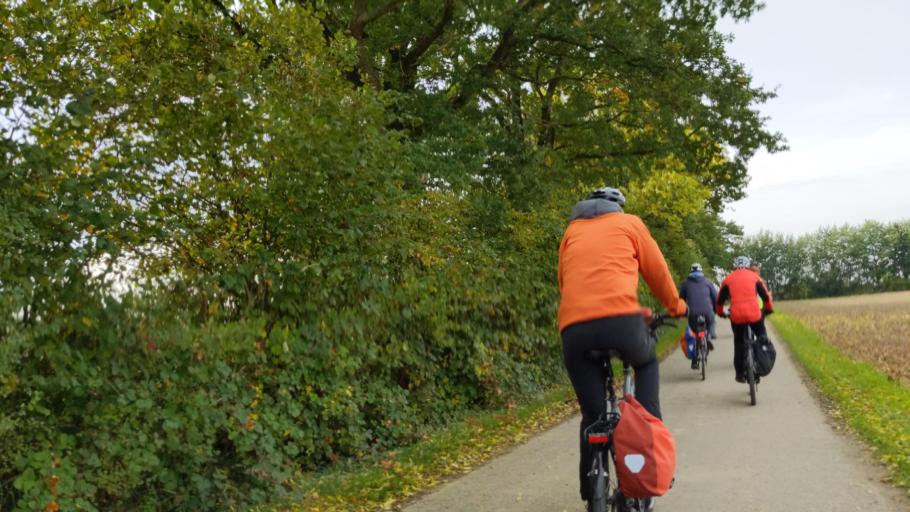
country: DE
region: Schleswig-Holstein
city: Rehhorst
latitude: 53.8825
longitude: 10.4908
